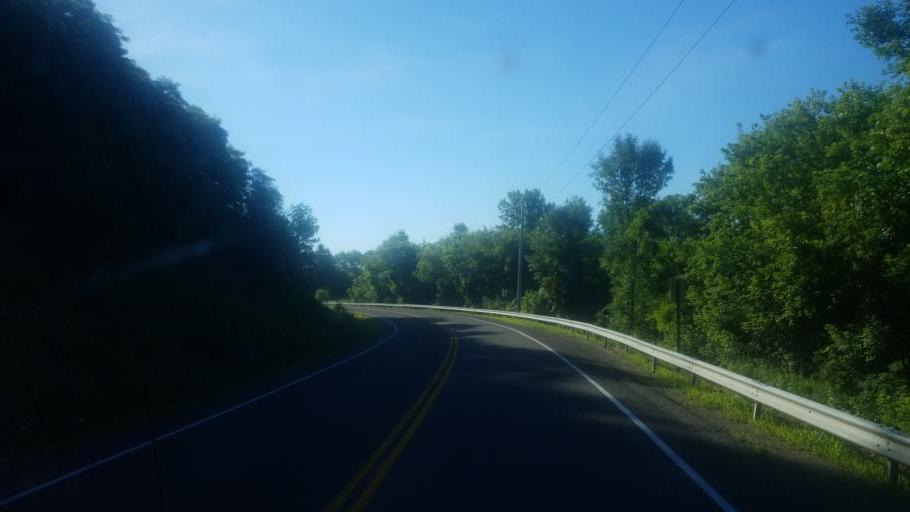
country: US
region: New York
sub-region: Wayne County
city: Lyons
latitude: 43.0793
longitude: -77.0322
